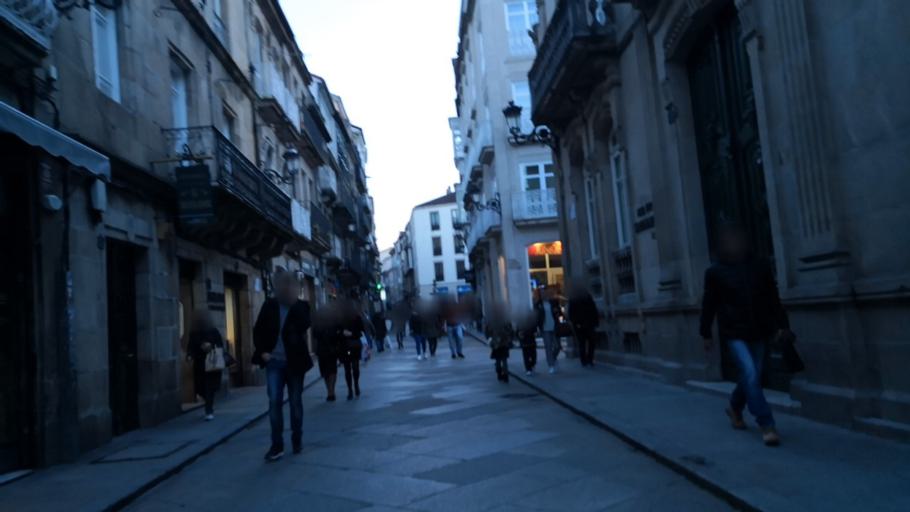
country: ES
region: Galicia
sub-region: Provincia de Ourense
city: Ourense
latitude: 42.3386
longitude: -7.8631
